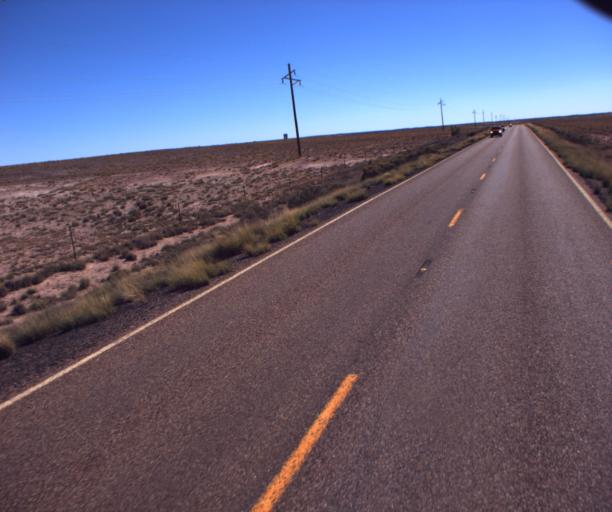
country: US
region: Arizona
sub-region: Navajo County
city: Holbrook
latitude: 35.0755
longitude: -110.0996
